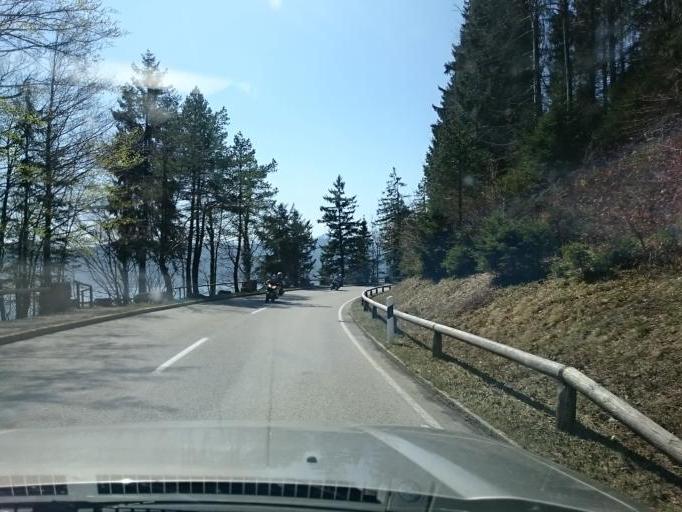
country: DE
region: Bavaria
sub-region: Upper Bavaria
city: Schlehdorf
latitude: 47.6099
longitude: 11.3381
